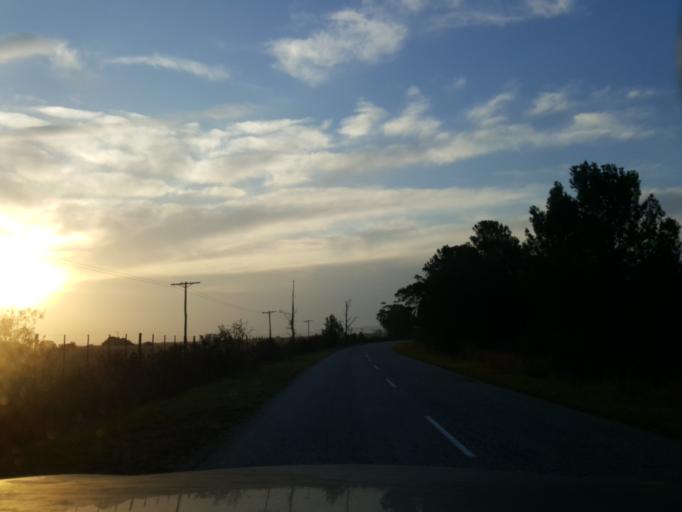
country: ZA
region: Eastern Cape
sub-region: Cacadu District Municipality
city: Grahamstown
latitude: -33.4495
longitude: 26.4879
